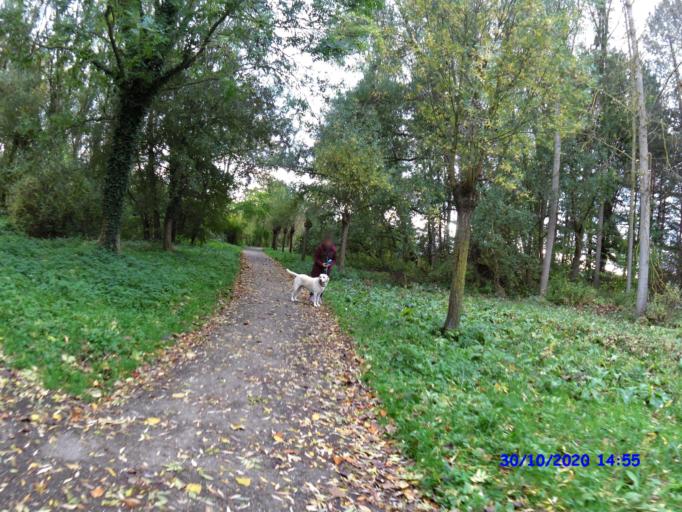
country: BE
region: Flanders
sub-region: Provincie Vlaams-Brabant
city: Landen
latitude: 50.7625
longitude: 5.0848
